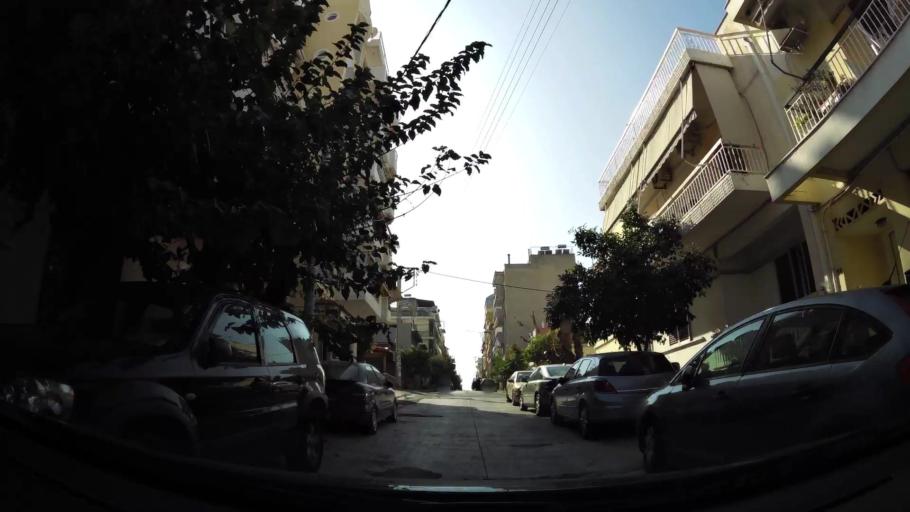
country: GR
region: Attica
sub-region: Nomos Piraios
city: Drapetsona
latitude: 37.9549
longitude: 23.6179
